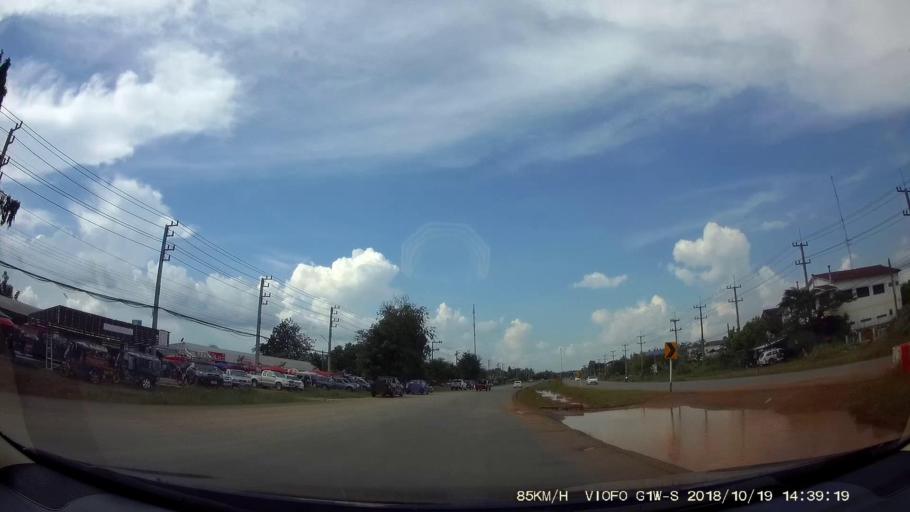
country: TH
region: Chaiyaphum
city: Kaeng Khro
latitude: 16.2244
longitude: 102.1954
